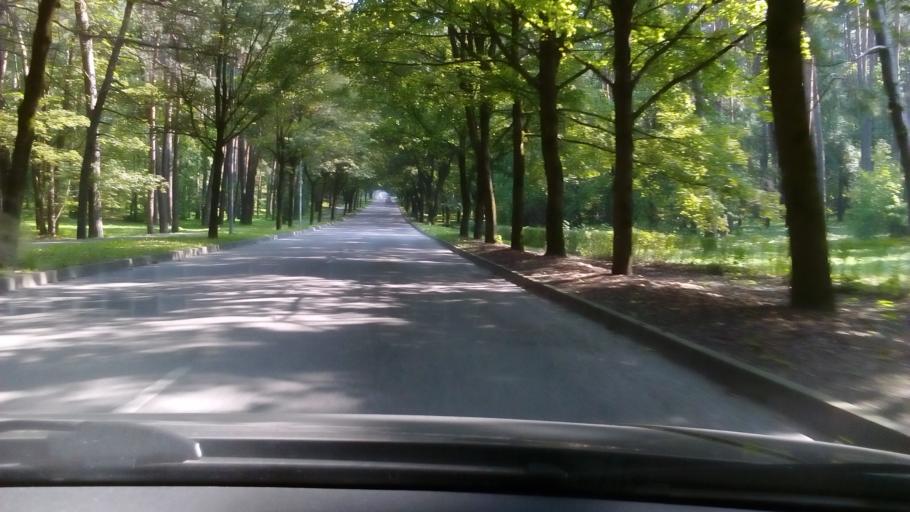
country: LT
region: Alytaus apskritis
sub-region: Alytus
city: Alytus
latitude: 54.3962
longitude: 24.0523
